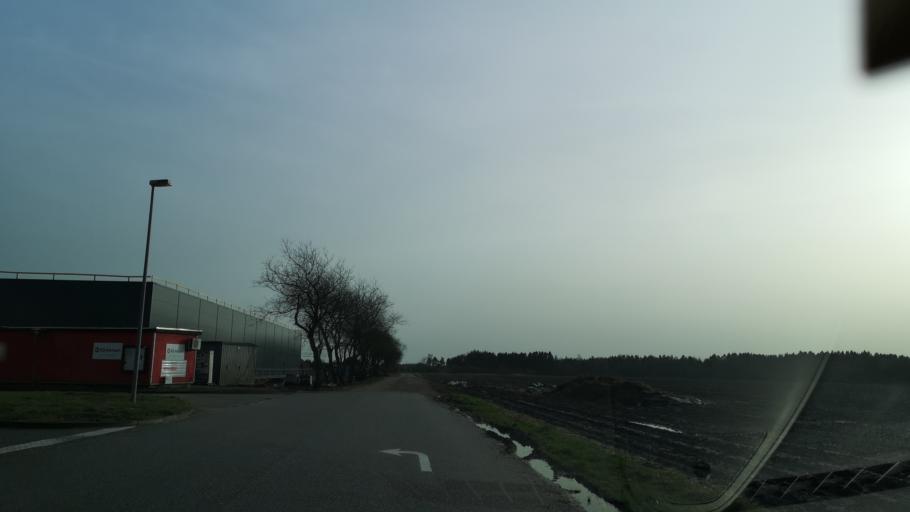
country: DK
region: Central Jutland
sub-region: Ikast-Brande Kommune
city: Brande
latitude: 56.0047
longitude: 9.1155
